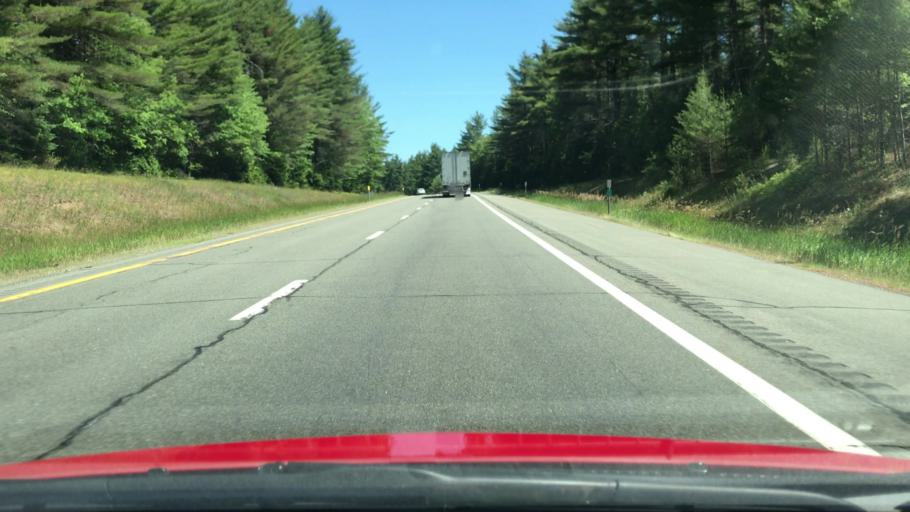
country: US
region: New York
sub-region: Essex County
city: Mineville
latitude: 43.9984
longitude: -73.7190
